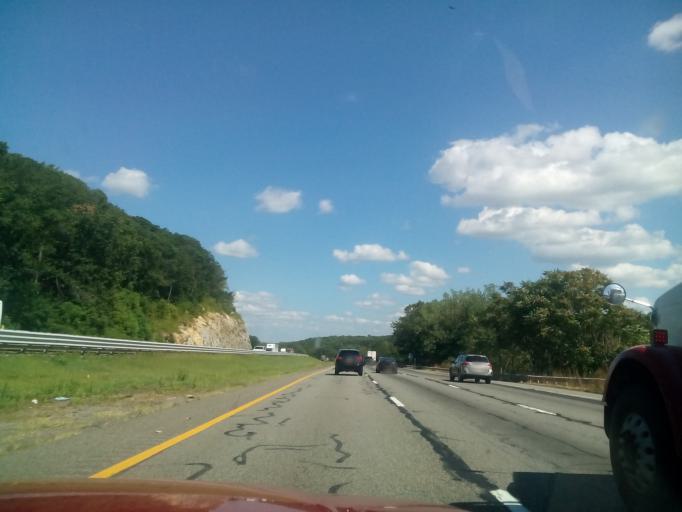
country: US
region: New Jersey
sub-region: Morris County
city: Succasunna
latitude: 40.8923
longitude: -74.6596
